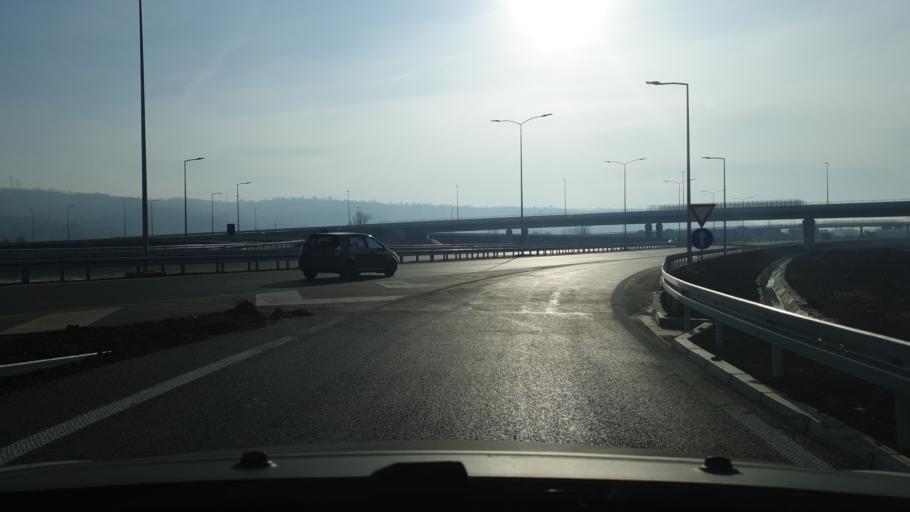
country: RS
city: Baric
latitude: 44.6533
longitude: 20.2327
